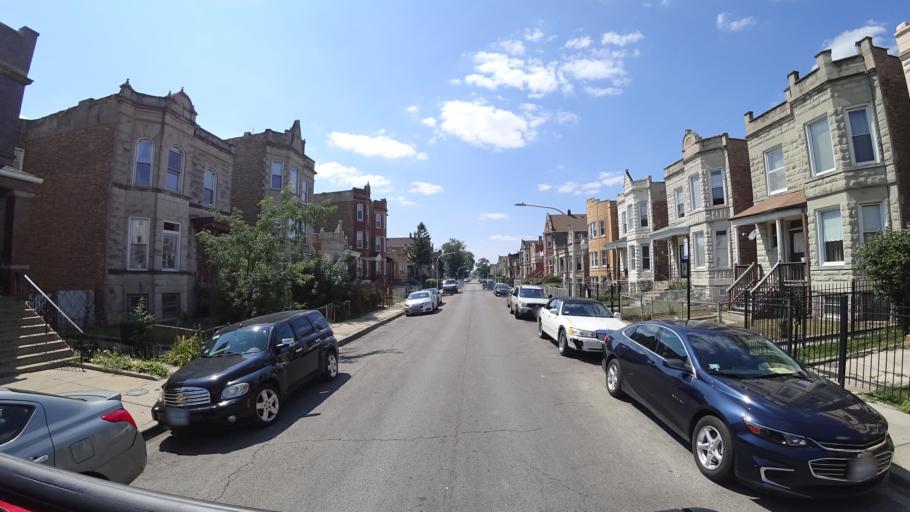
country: US
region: Illinois
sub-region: Cook County
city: Cicero
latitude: 41.8526
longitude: -87.7257
